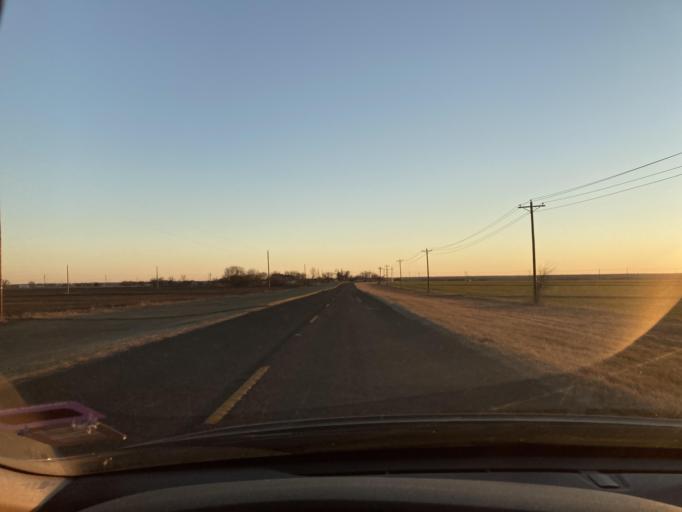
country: US
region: Texas
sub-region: Ellis County
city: Nash
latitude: 32.2840
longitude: -96.8989
